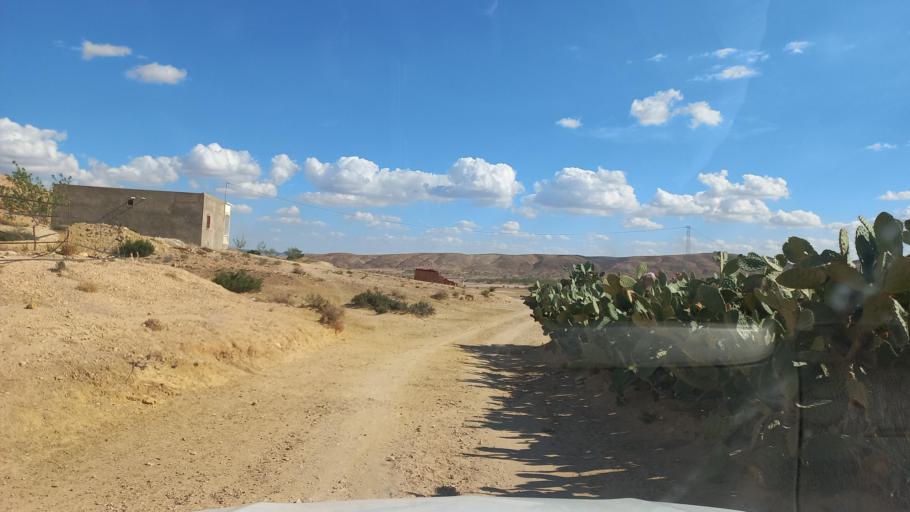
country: TN
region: Al Qasrayn
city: Sbiba
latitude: 35.4055
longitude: 8.9977
